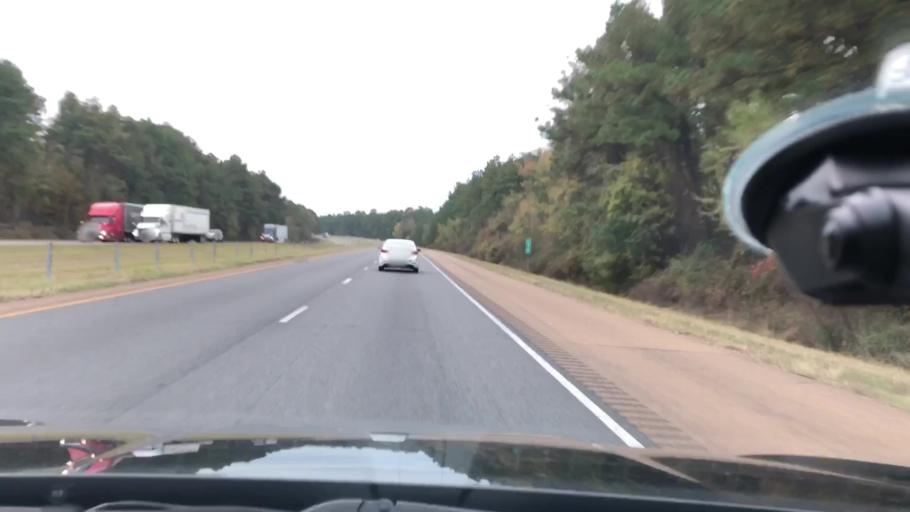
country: US
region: Arkansas
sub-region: Clark County
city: Gurdon
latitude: 33.9549
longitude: -93.2274
